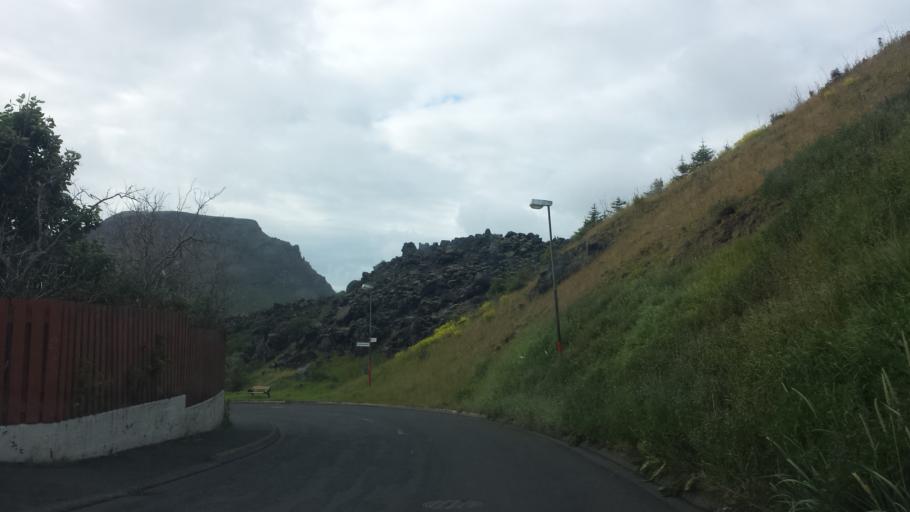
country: IS
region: South
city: Vestmannaeyjar
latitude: 63.4404
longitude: -20.2631
